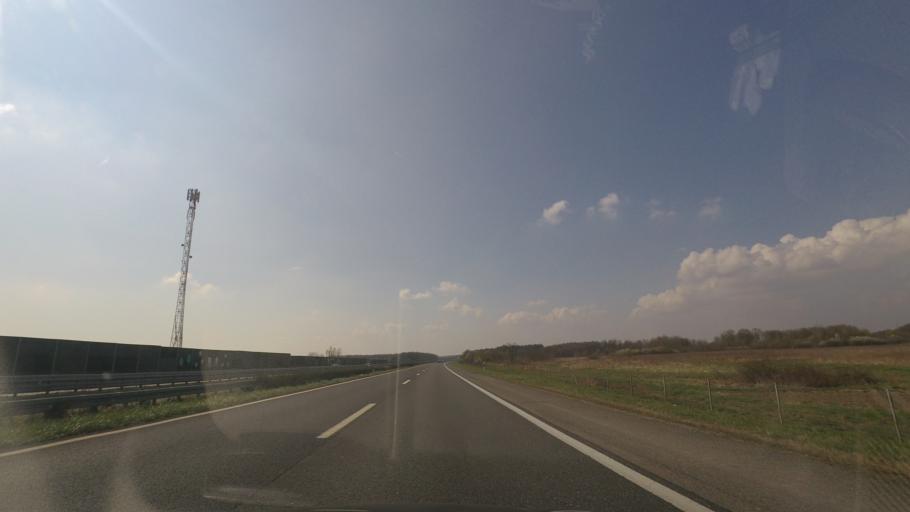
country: HR
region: Grad Zagreb
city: Brezovica
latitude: 45.7343
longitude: 15.8763
